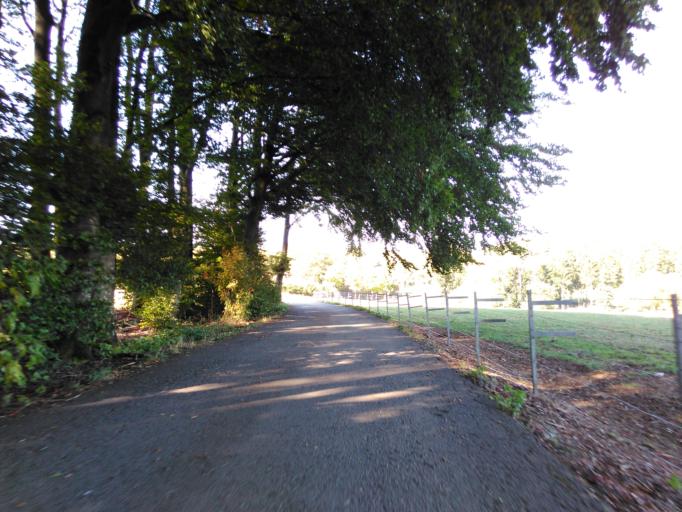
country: LU
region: Diekirch
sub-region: Canton de Redange
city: Rambrouch
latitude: 49.8105
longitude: 5.8427
